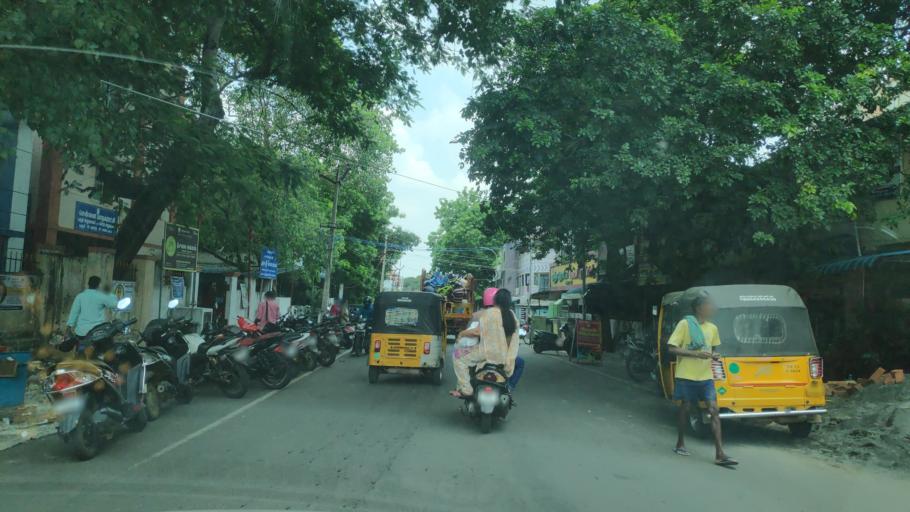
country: IN
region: Tamil Nadu
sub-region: Thiruvallur
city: Ambattur
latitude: 13.1178
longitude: 80.1540
